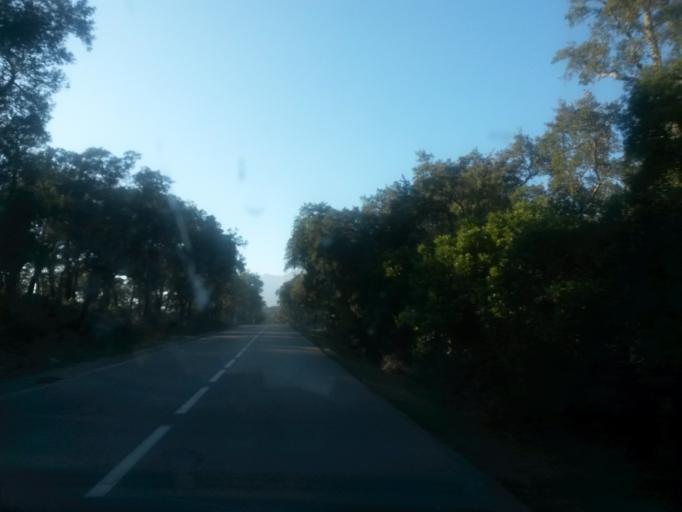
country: ES
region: Catalonia
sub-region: Provincia de Girona
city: Darnius
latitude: 42.3720
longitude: 2.8089
